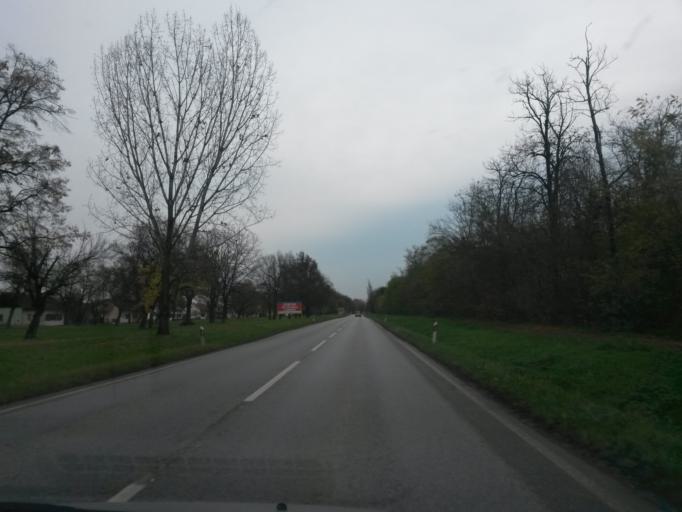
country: HR
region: Osjecko-Baranjska
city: Darda
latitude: 45.6217
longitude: 18.7135
